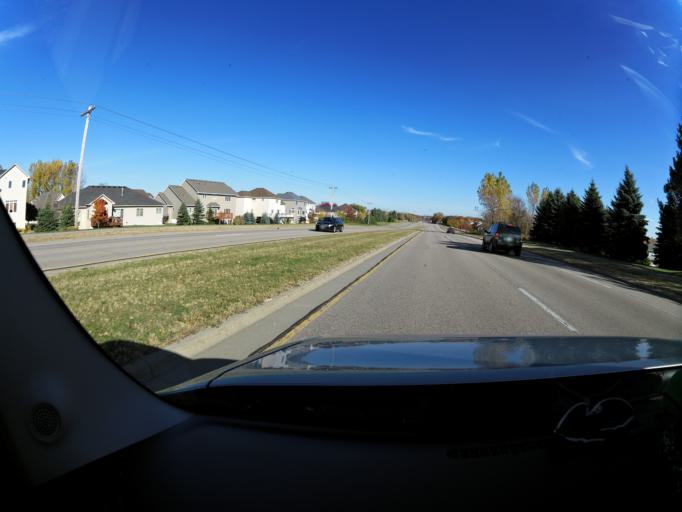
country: US
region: Minnesota
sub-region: Scott County
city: Prior Lake
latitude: 44.7248
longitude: -93.4559
